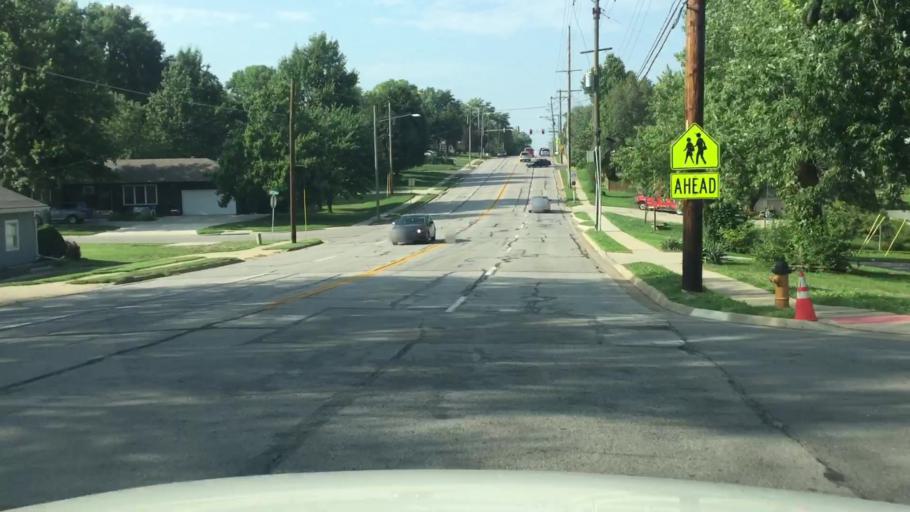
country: US
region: Kansas
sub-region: Johnson County
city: Shawnee
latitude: 39.0371
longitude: -94.7145
